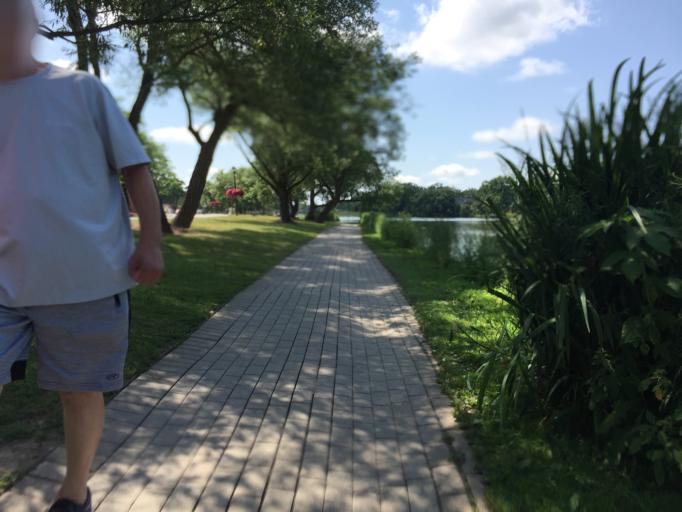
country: CA
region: Ontario
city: Stratford
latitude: 43.3749
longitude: -80.9756
